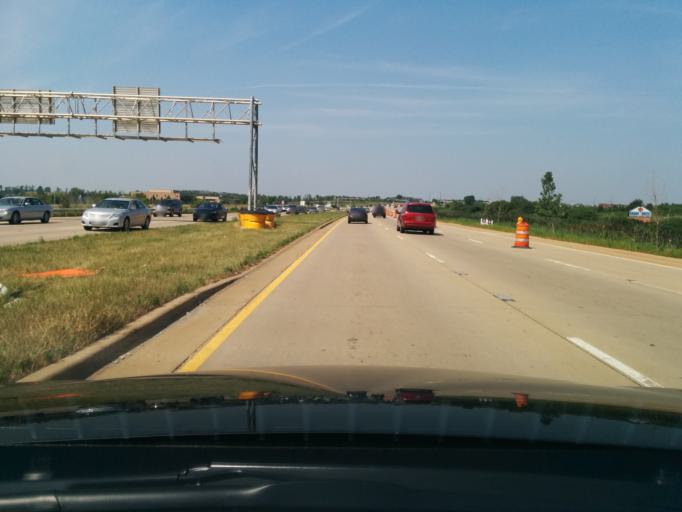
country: US
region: Illinois
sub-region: Cook County
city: Orland Hills
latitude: 41.5568
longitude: -87.8534
